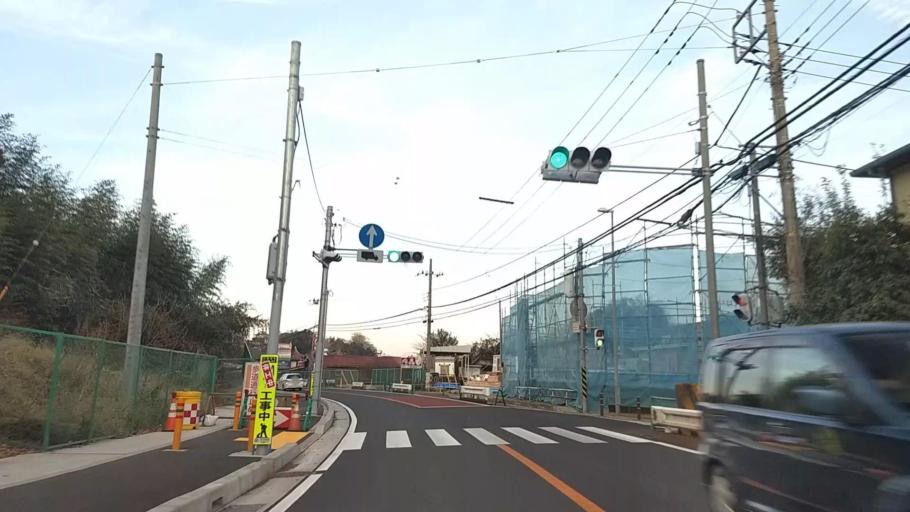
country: JP
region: Kanagawa
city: Atsugi
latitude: 35.4418
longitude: 139.3264
